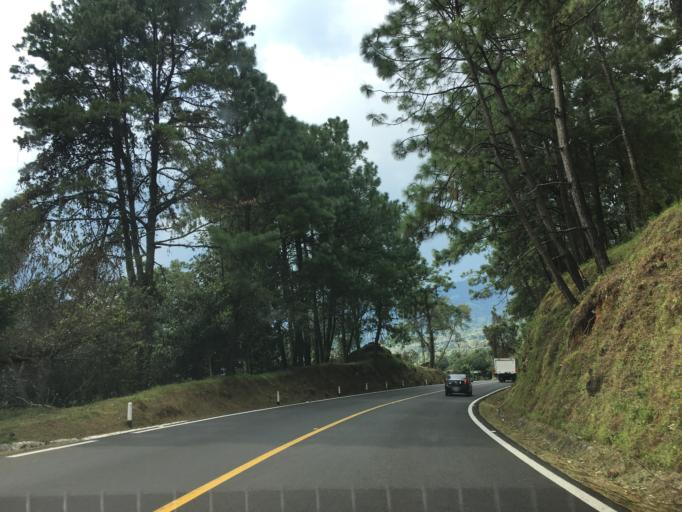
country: MX
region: Michoacan
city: Tingambato
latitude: 19.4958
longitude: -101.8376
